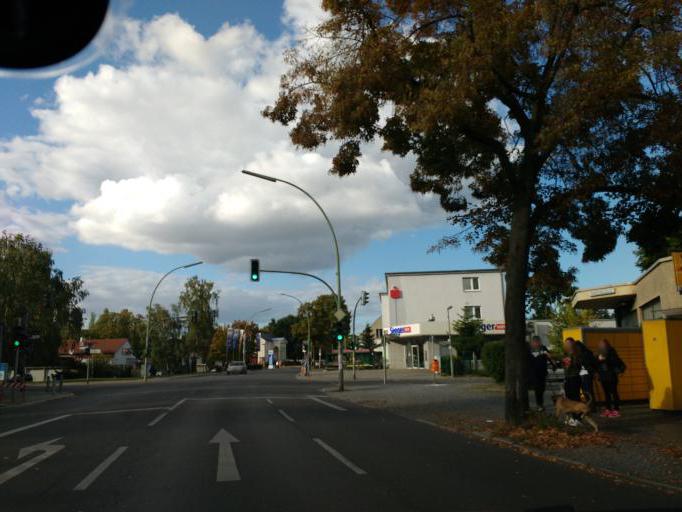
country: DE
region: Berlin
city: Britz
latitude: 52.4246
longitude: 13.4358
